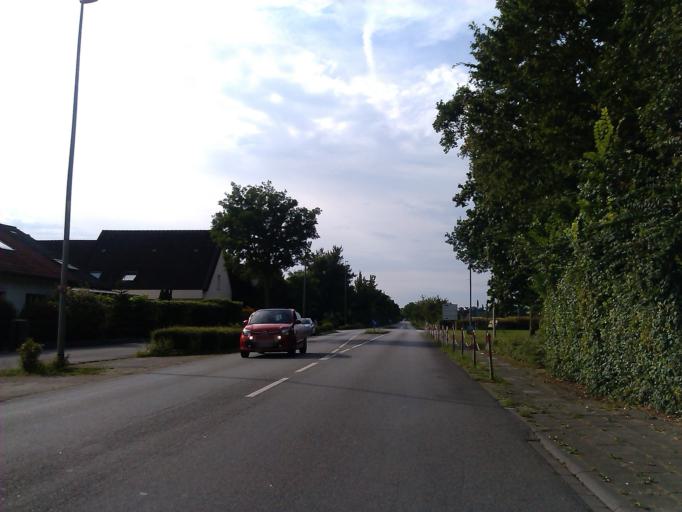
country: DE
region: Rheinland-Pfalz
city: Limburgerhof
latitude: 49.4168
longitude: 8.3980
